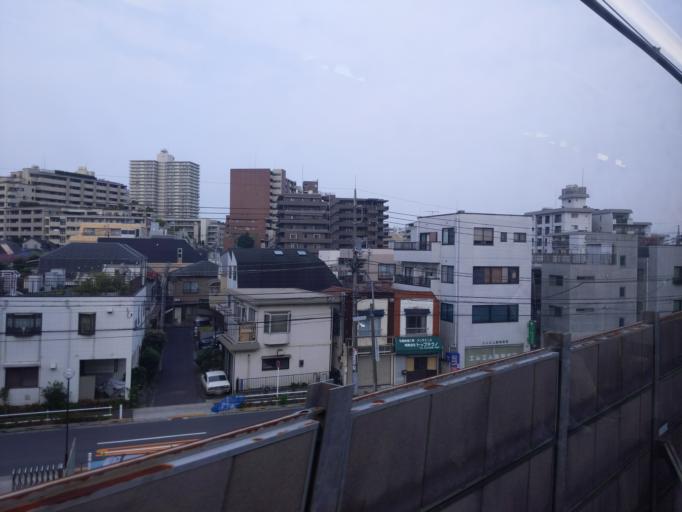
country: JP
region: Saitama
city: Shimotoda
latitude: 35.7774
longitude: 139.6824
